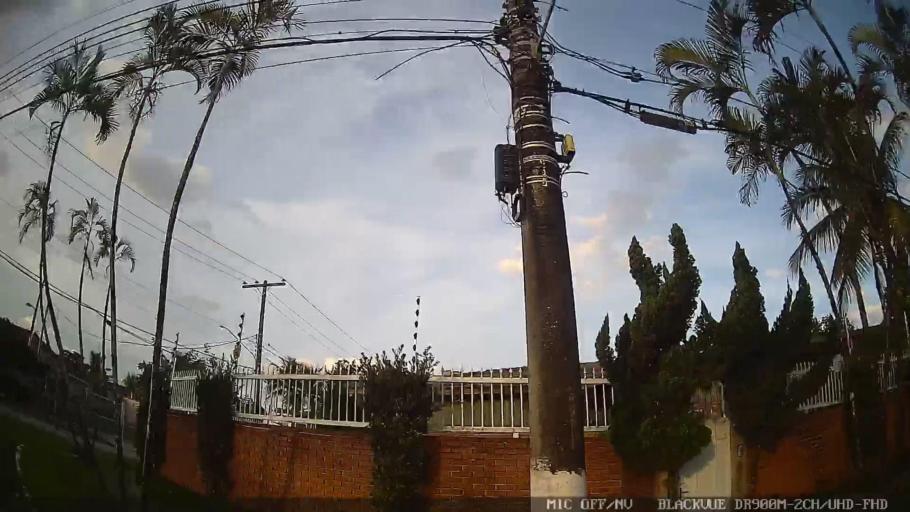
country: BR
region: Sao Paulo
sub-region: Guaruja
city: Guaruja
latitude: -23.9812
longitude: -46.2116
